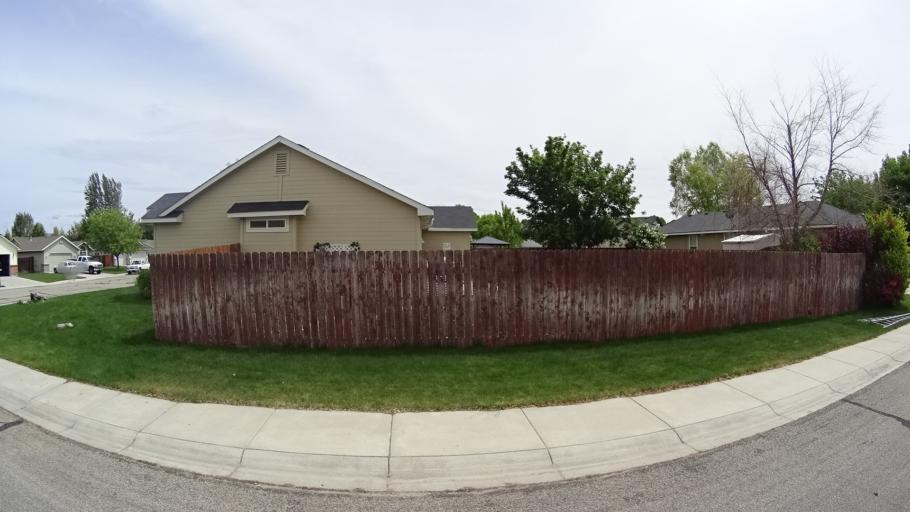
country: US
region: Idaho
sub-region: Ada County
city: Meridian
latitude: 43.5562
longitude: -116.3372
